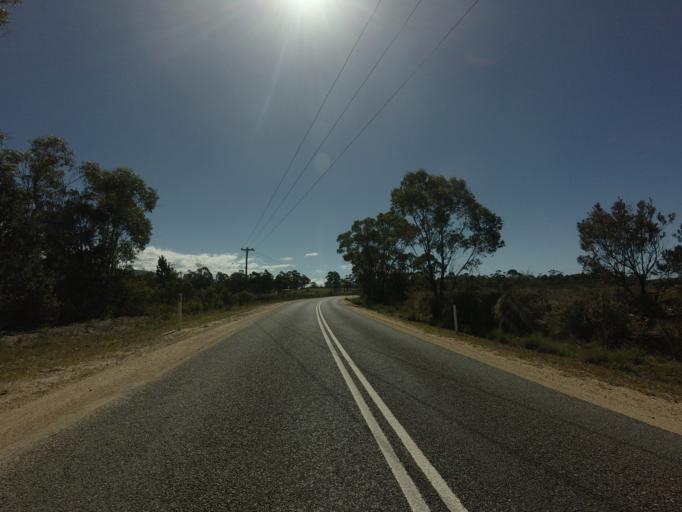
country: AU
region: Tasmania
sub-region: Break O'Day
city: St Helens
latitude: -41.8354
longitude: 148.2547
